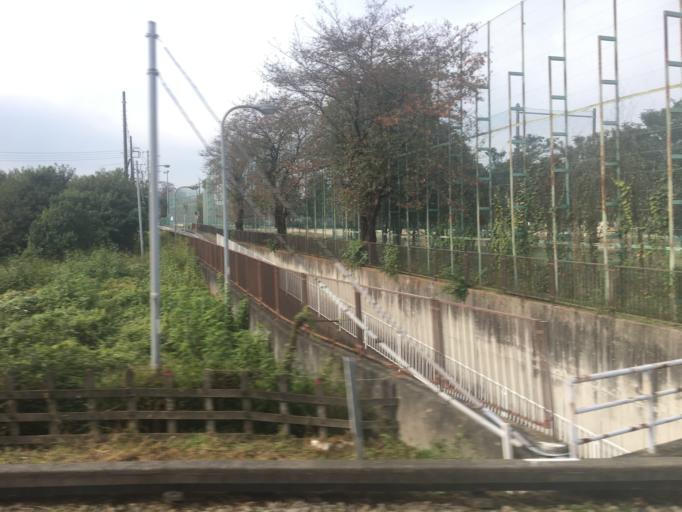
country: JP
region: Saitama
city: Sayama
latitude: 35.8393
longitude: 139.4218
